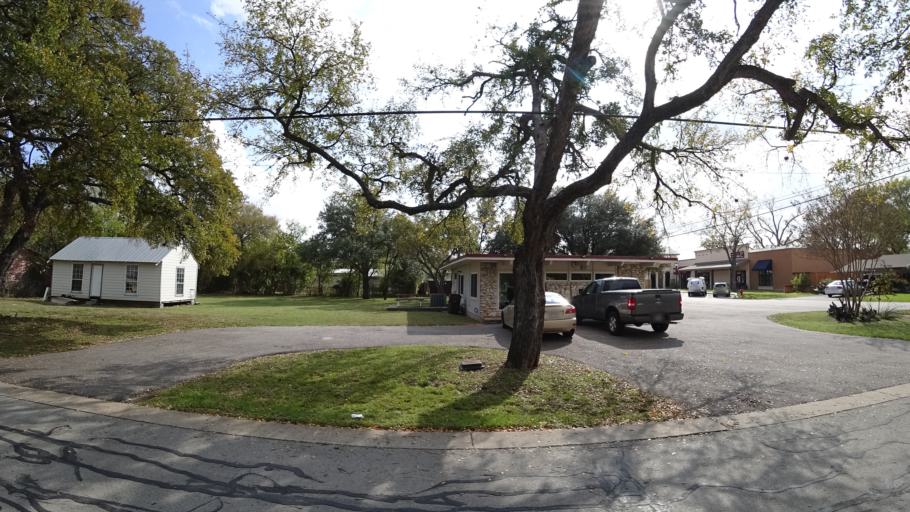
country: US
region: Texas
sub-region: Williamson County
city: Round Rock
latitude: 30.5122
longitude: -97.6787
